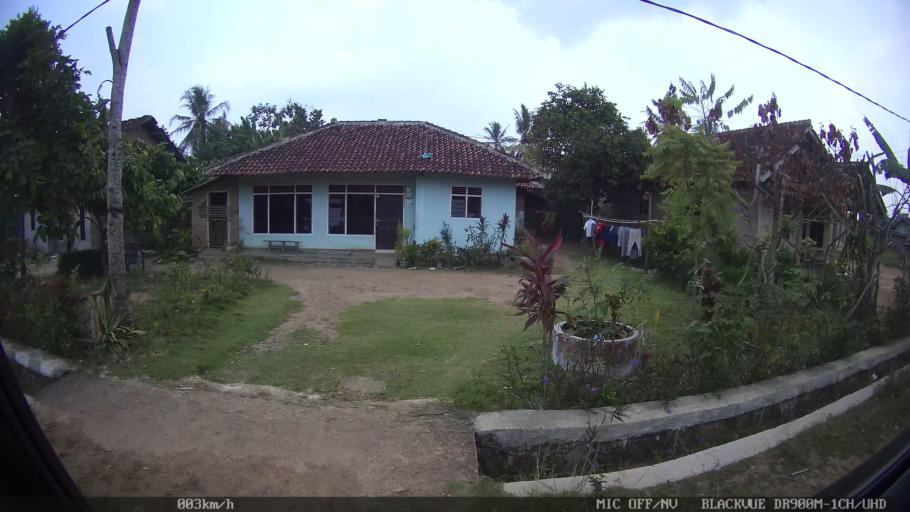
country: ID
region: Lampung
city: Gadingrejo
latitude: -5.3929
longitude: 105.0370
